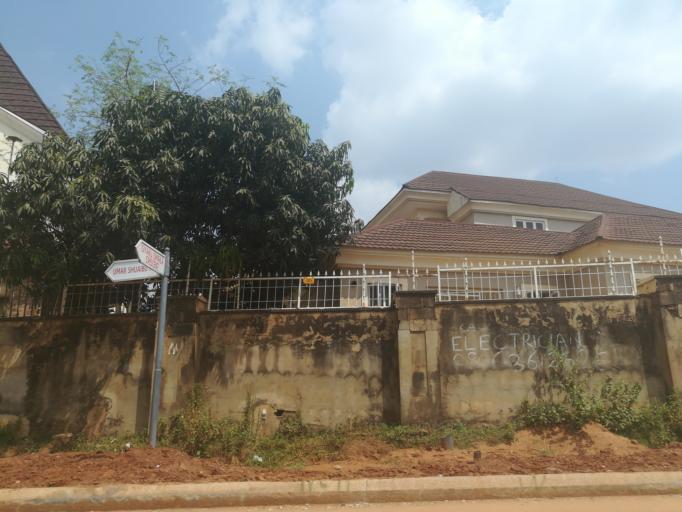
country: NG
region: Abuja Federal Capital Territory
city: Abuja
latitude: 9.0576
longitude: 7.4474
